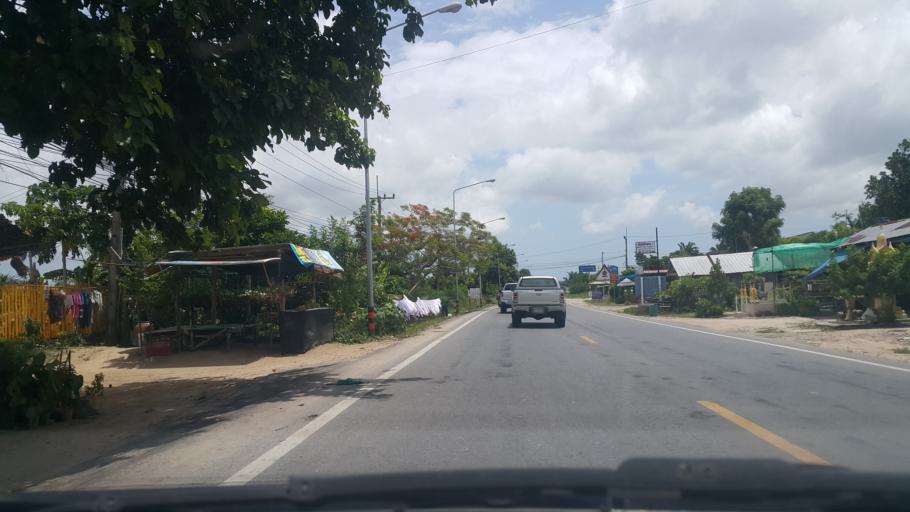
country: TH
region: Rayong
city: Ban Chang
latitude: 12.7568
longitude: 101.0332
